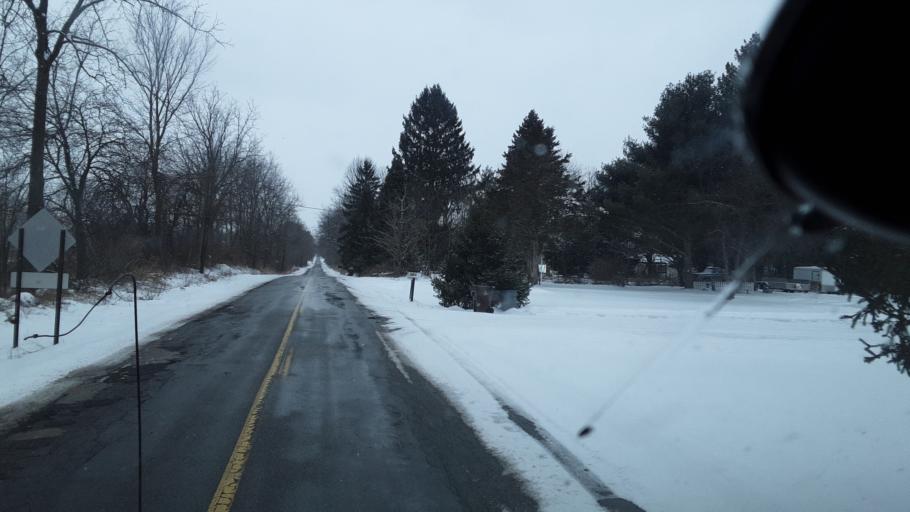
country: US
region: Michigan
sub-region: Ingham County
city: Leslie
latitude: 42.4367
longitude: -84.4463
